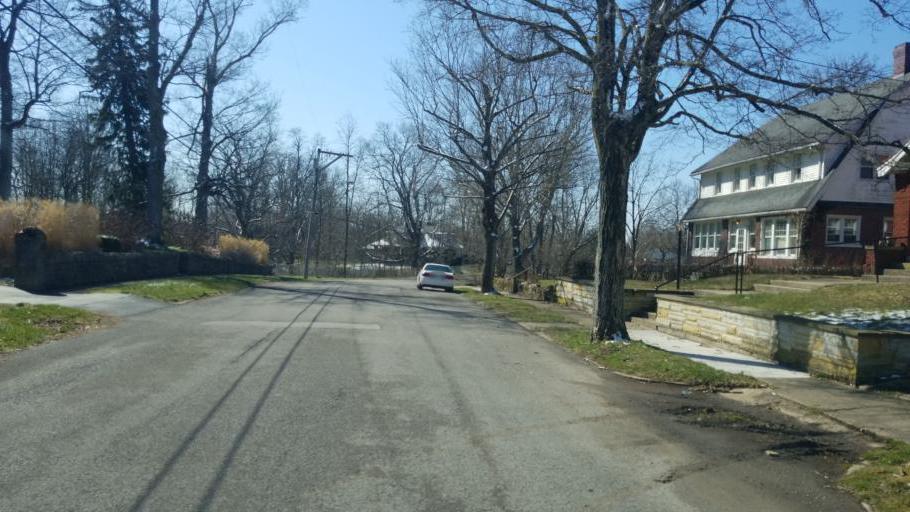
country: US
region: Ohio
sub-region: Highland County
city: Greenfield
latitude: 39.3444
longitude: -83.3805
